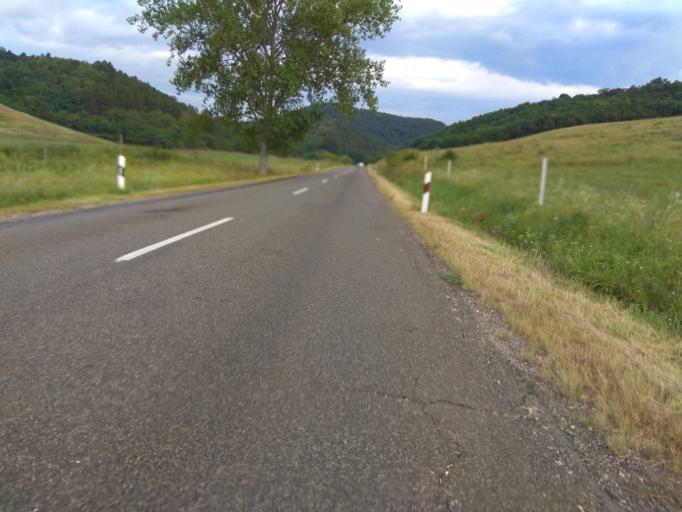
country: HU
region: Heves
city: Tarnalelesz
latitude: 48.0609
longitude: 20.2000
